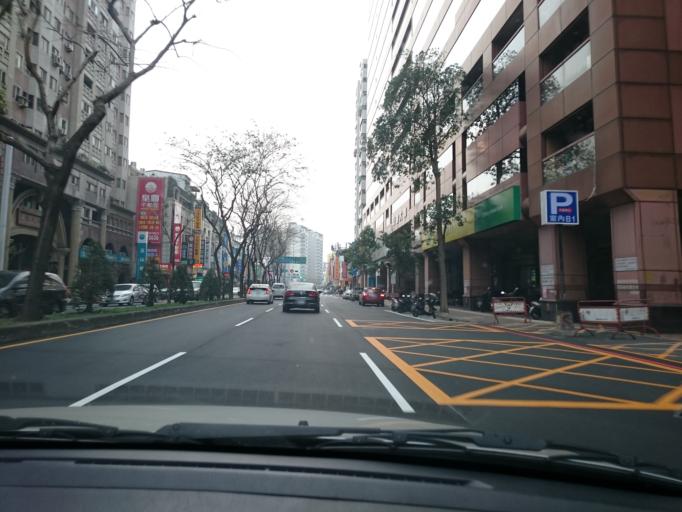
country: TW
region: Taiwan
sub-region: Taichung City
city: Taichung
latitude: 24.1419
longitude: 120.6396
